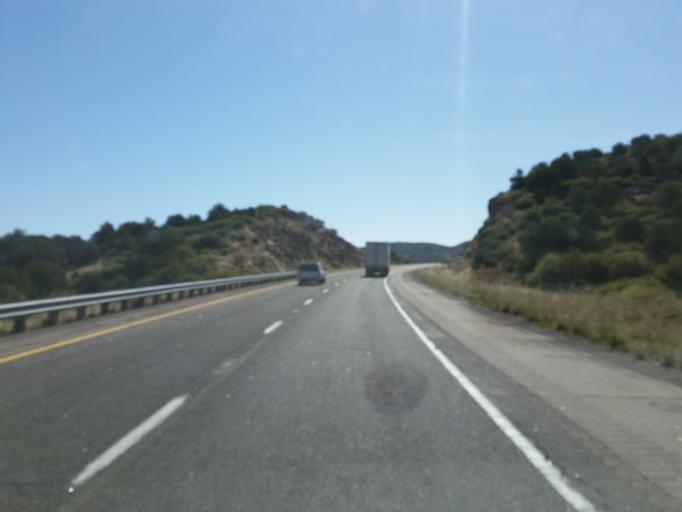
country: US
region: Arizona
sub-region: Mohave County
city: Peach Springs
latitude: 35.1808
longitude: -113.4676
